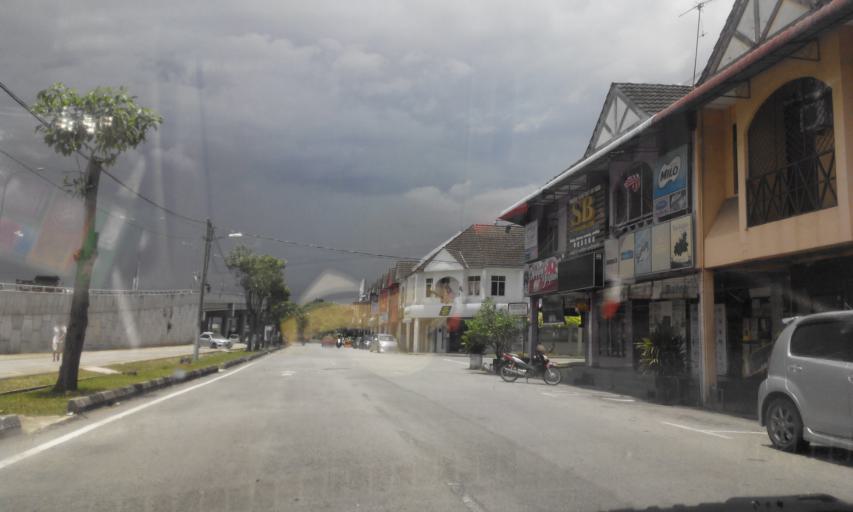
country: MY
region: Perak
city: Parit Buntar
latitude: 5.1207
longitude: 100.4869
